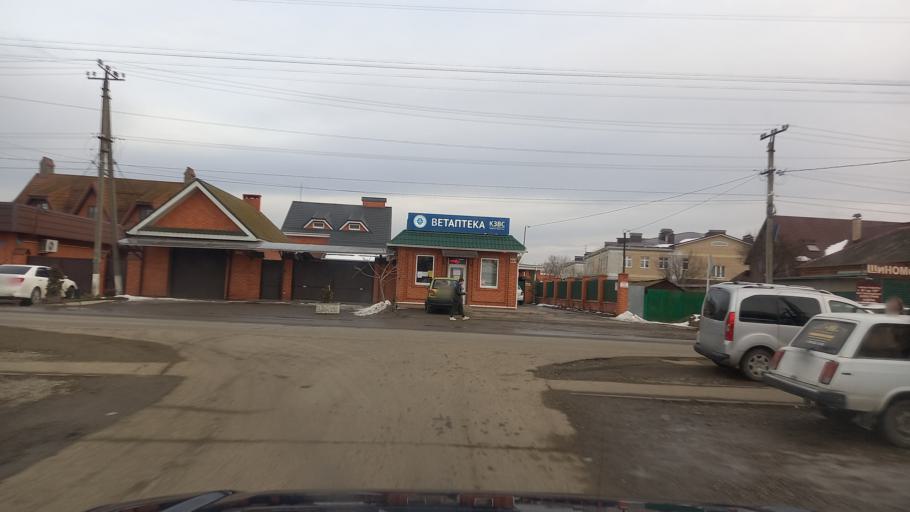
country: RU
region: Krasnodarskiy
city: Belorechensk
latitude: 44.7723
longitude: 39.8647
